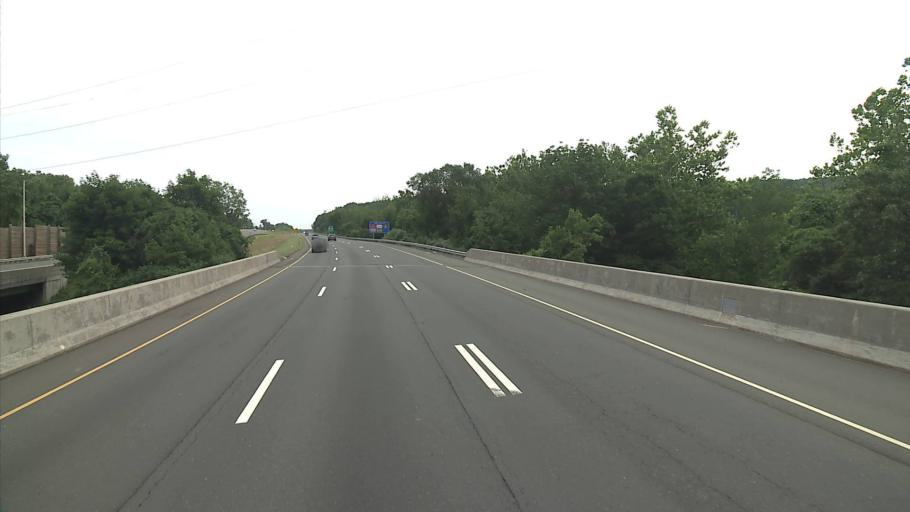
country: US
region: Connecticut
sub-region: New Haven County
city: Southbury
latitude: 41.4661
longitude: -73.2215
